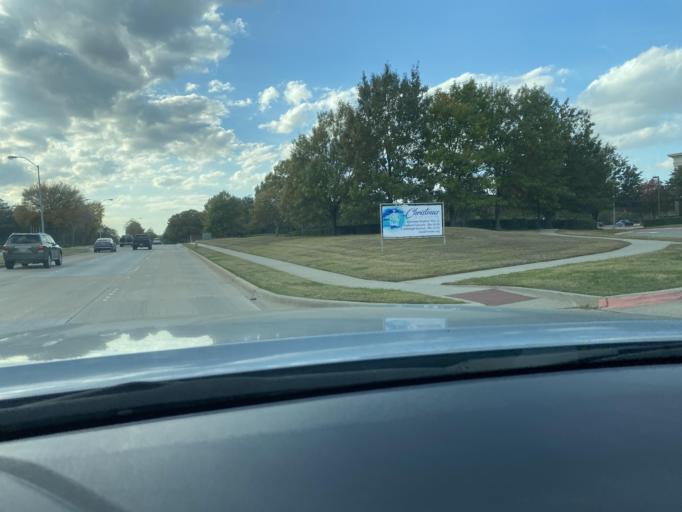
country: US
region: Texas
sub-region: Dallas County
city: Addison
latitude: 33.0168
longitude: -96.8193
